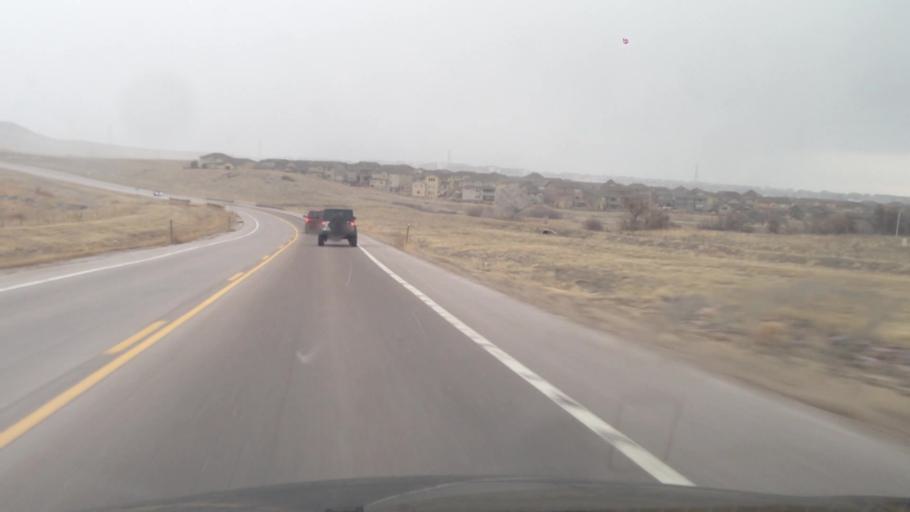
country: US
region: Colorado
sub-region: Douglas County
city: Stonegate
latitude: 39.4970
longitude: -104.8173
